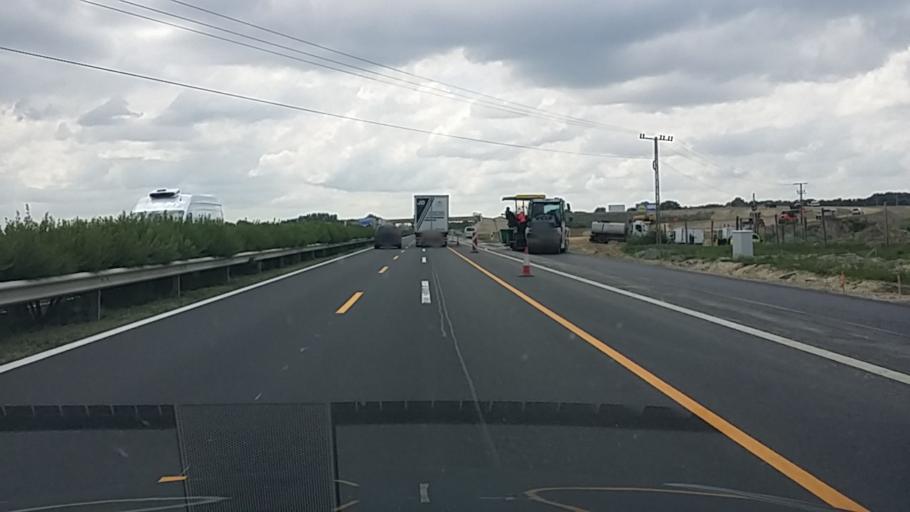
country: HU
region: Bacs-Kiskun
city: Kecskemet
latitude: 46.9360
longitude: 19.6184
